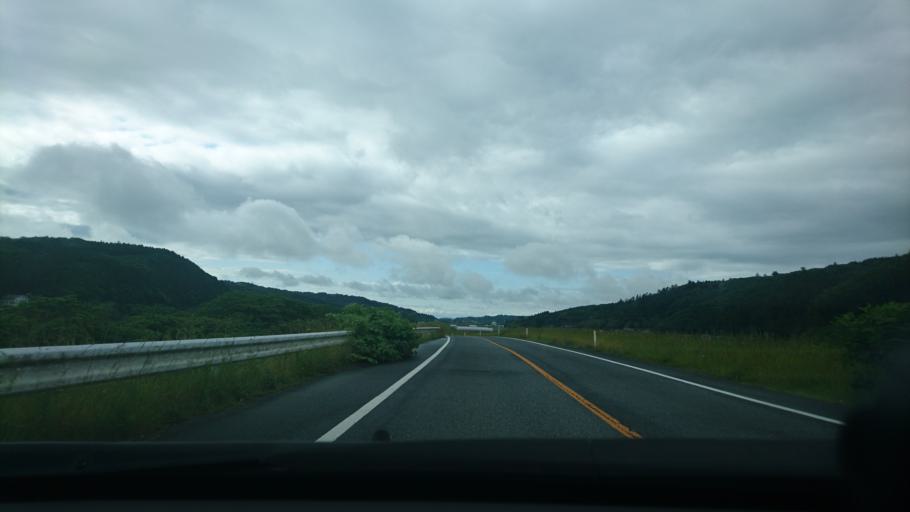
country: JP
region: Miyagi
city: Wakuya
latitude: 38.6246
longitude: 141.2953
